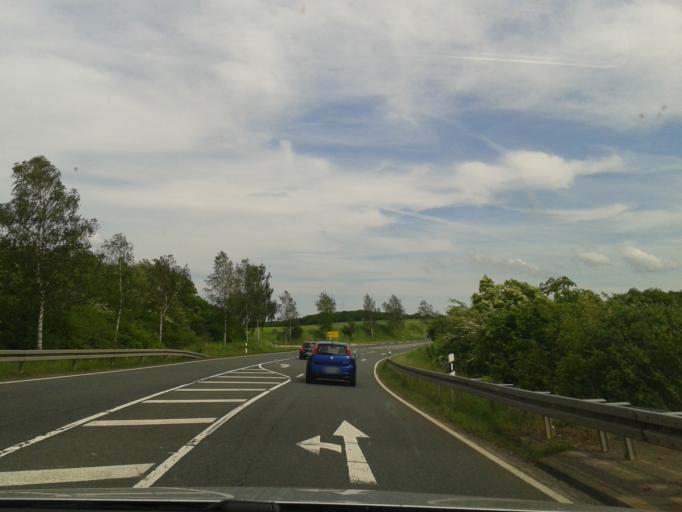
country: DE
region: Hesse
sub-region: Regierungsbezirk Giessen
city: Lohra
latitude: 50.7614
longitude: 8.6664
